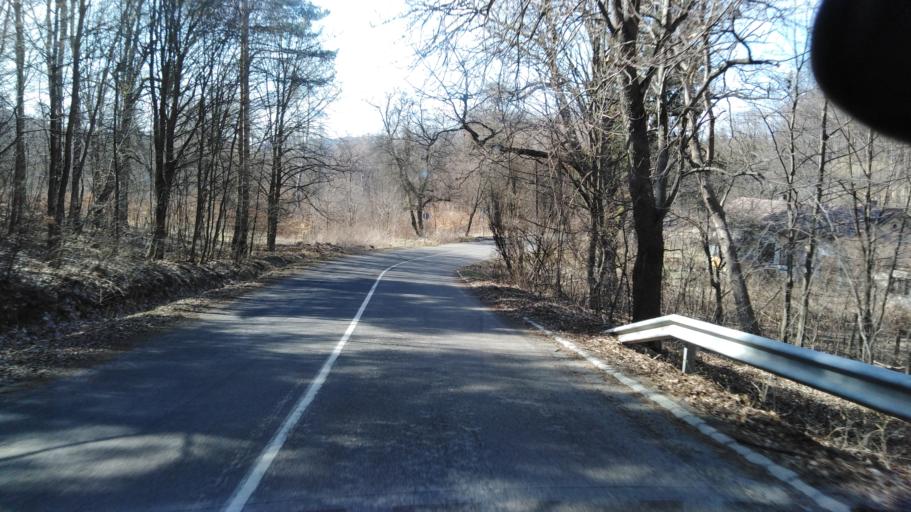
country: HU
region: Nograd
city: Somoskoujfalu
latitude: 48.1512
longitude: 19.8626
